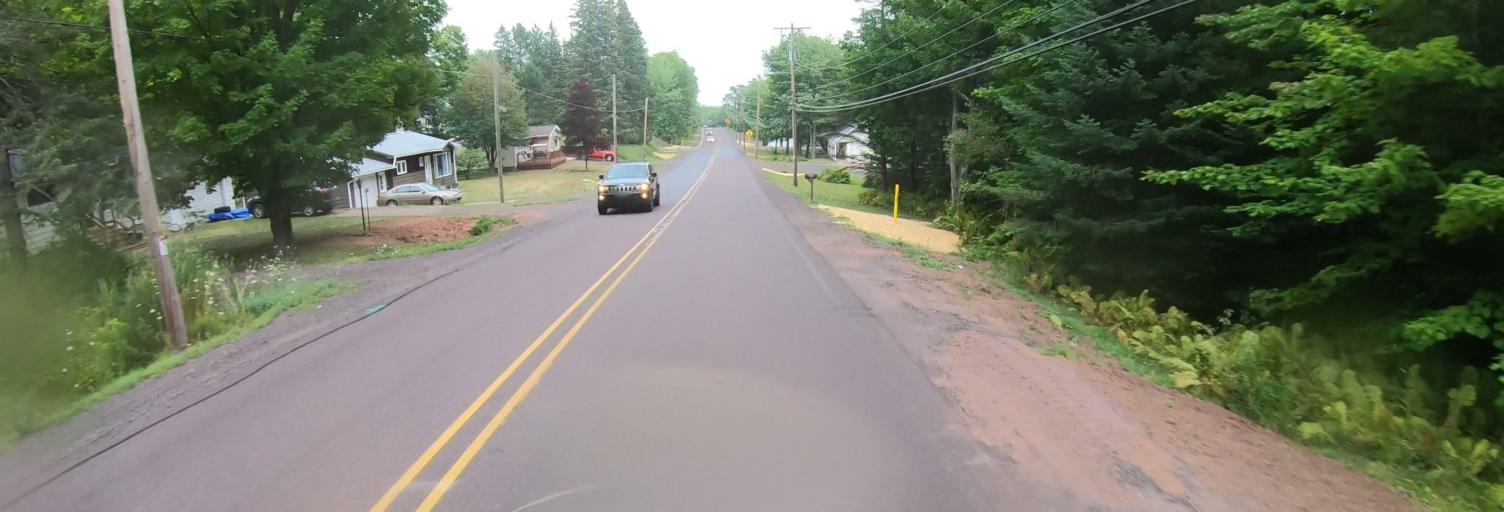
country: US
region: Michigan
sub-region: Houghton County
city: Dollar Bay
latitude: 47.0254
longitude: -88.5320
